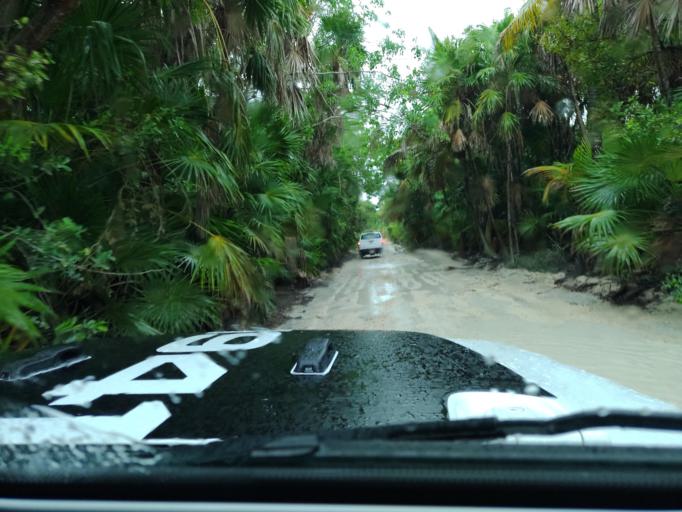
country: MX
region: Quintana Roo
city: Tulum
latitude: 19.9739
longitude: -87.4689
